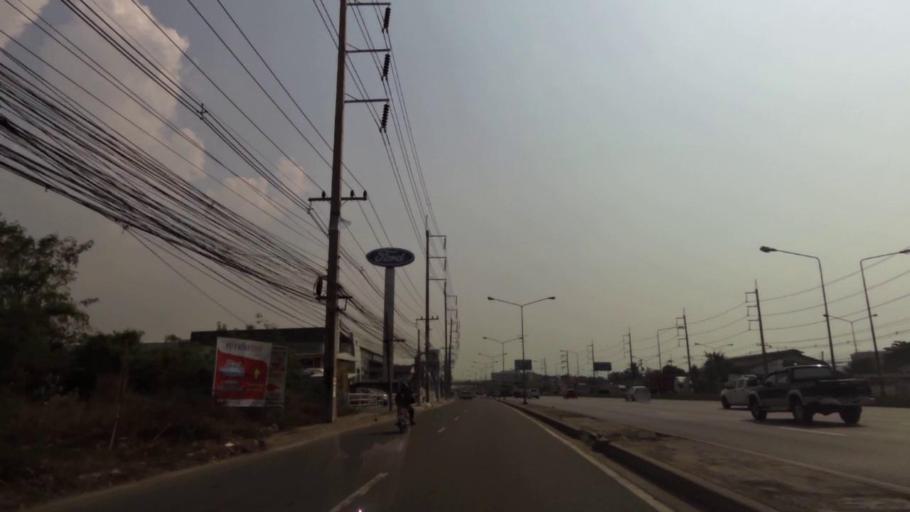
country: TH
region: Chon Buri
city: Chon Buri
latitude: 13.4037
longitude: 101.0032
